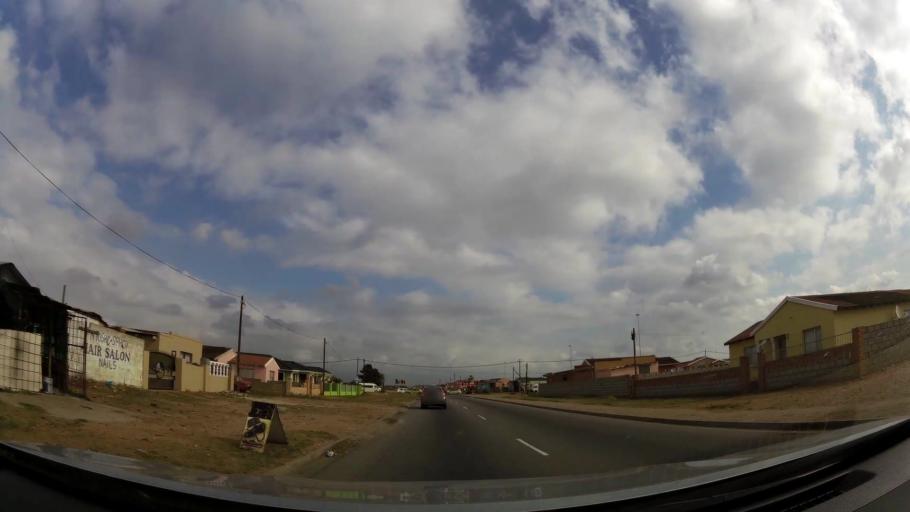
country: ZA
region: Eastern Cape
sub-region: Nelson Mandela Bay Metropolitan Municipality
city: Port Elizabeth
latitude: -33.8164
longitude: 25.5842
